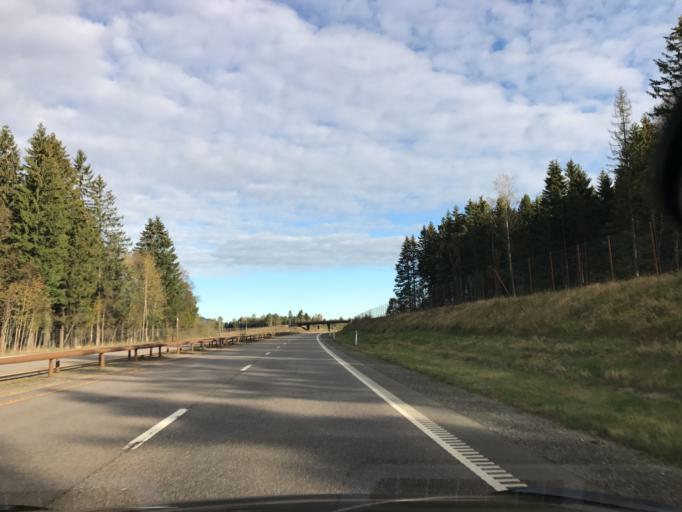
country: NO
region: Akershus
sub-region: Eidsvoll
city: Eidsvoll
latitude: 60.3663
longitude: 11.2041
